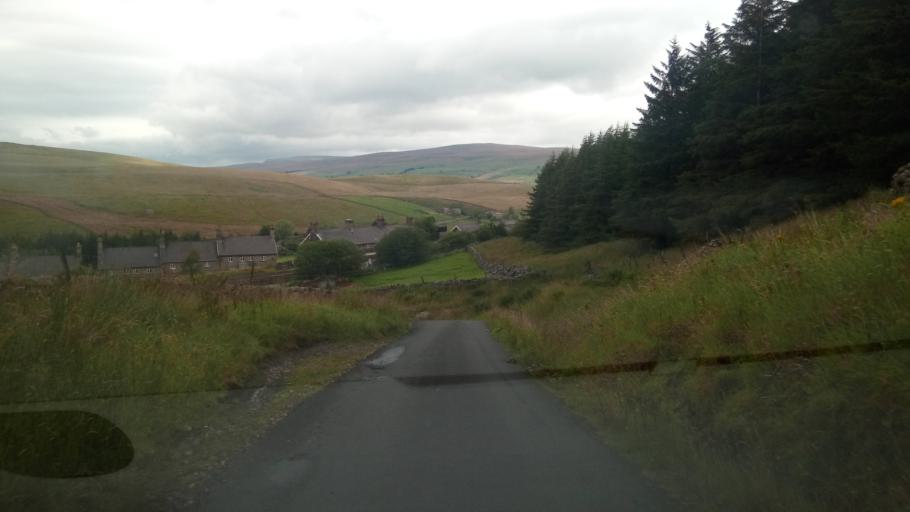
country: GB
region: England
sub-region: Cumbria
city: Kirkby Stephen
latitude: 54.3199
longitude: -2.3275
